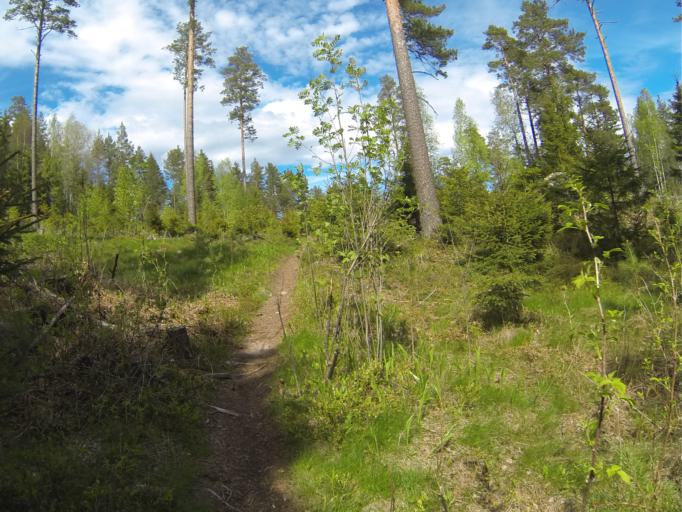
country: FI
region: Varsinais-Suomi
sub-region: Salo
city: Halikko
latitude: 60.3462
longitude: 23.0902
